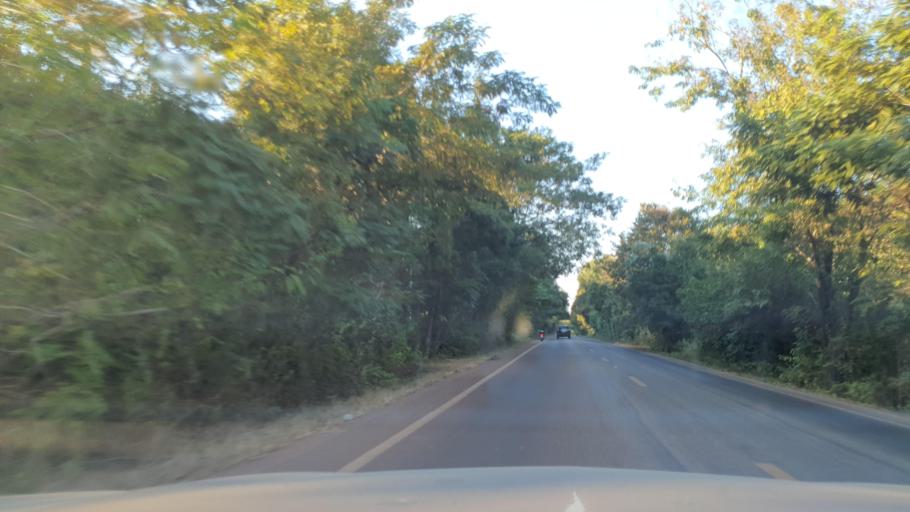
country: TH
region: Nakhon Phanom
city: Si Songkhram
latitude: 17.5619
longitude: 104.2366
